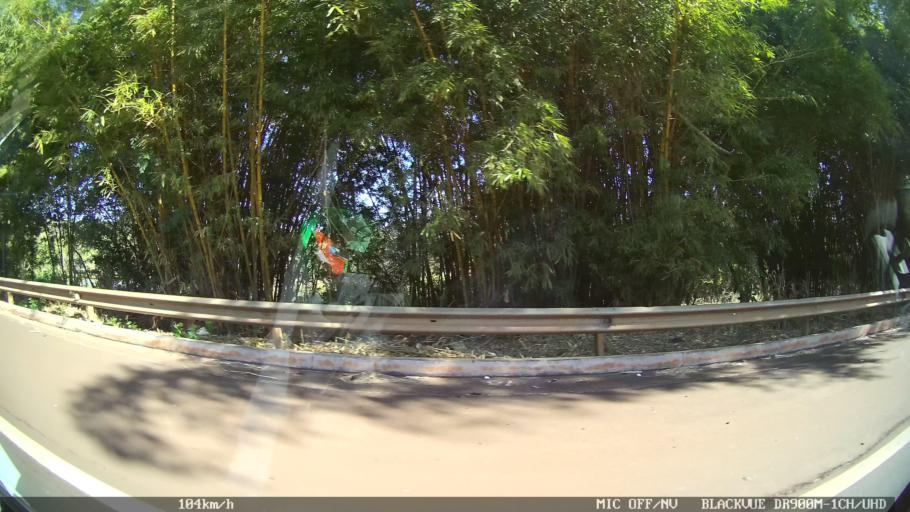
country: BR
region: Sao Paulo
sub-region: Olimpia
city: Olimpia
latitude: -20.7012
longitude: -48.8888
